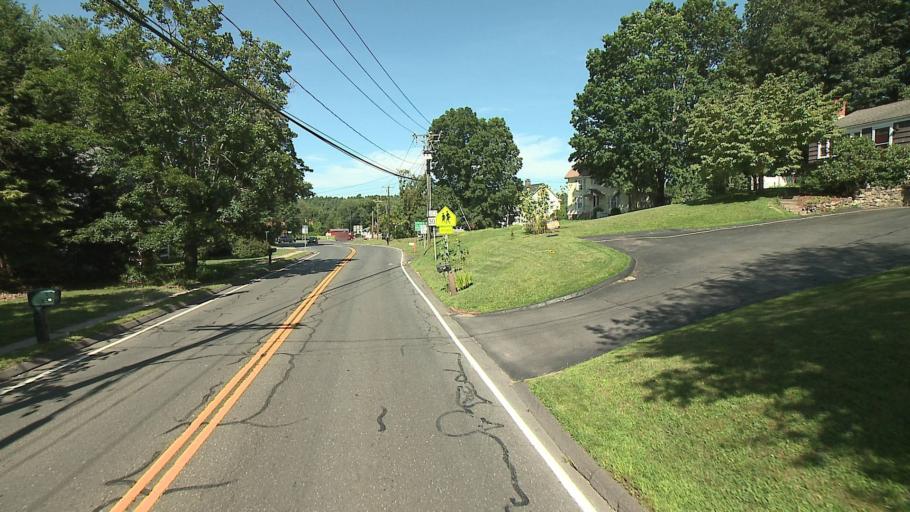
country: US
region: Connecticut
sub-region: Hartford County
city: Simsbury Center
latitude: 41.8689
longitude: -72.8188
